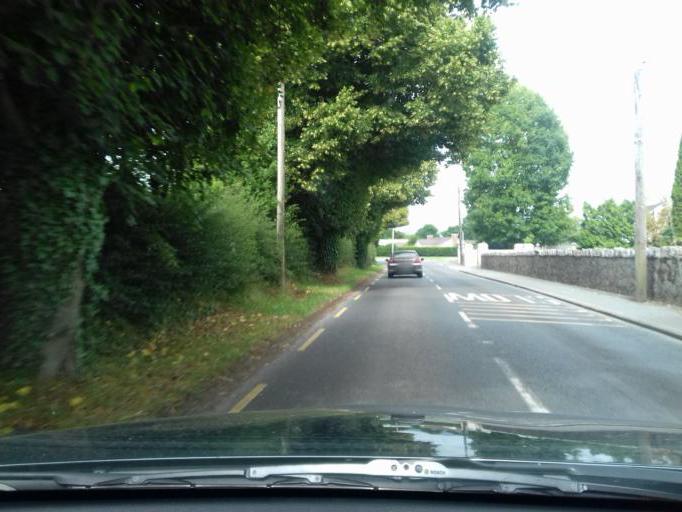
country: IE
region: Leinster
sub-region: Wicklow
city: Baltinglass
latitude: 52.8785
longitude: -6.6976
